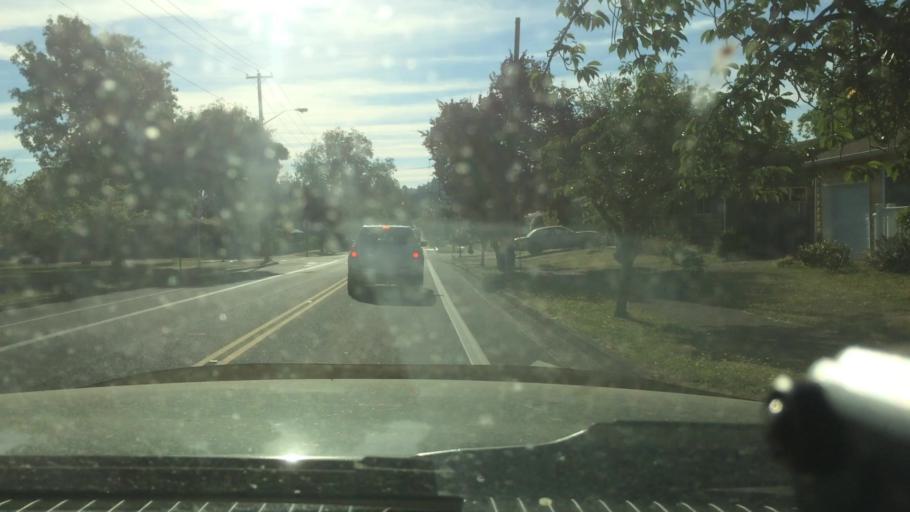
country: US
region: Oregon
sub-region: Lane County
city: Eugene
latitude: 44.0330
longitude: -123.1131
